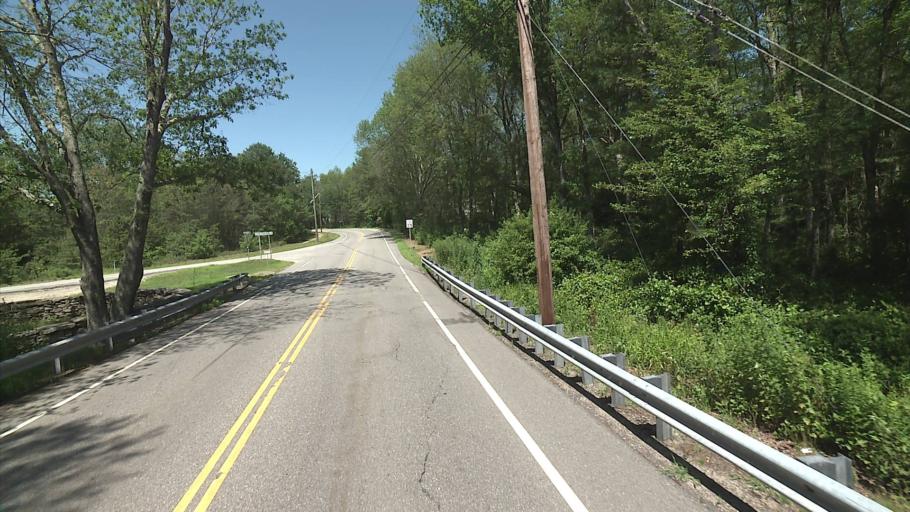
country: US
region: Connecticut
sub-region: Windham County
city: Moosup
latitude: 41.7029
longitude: -71.8103
